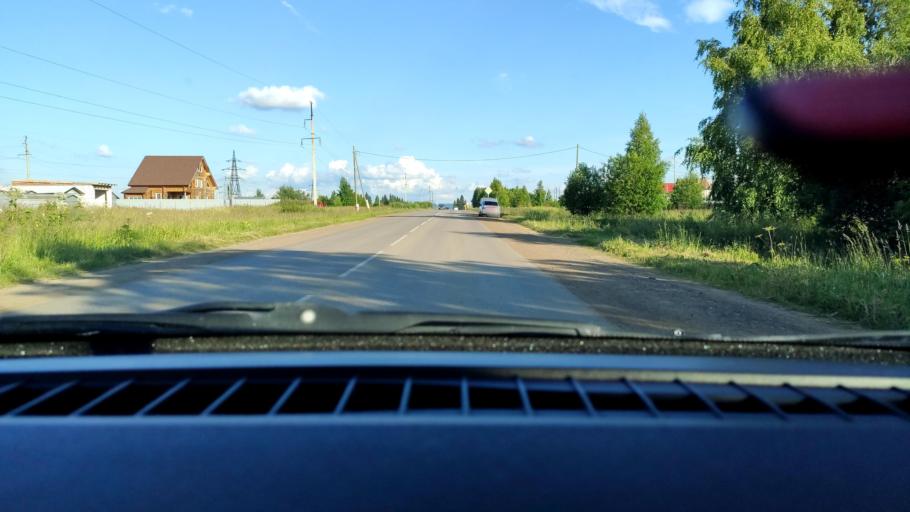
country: RU
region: Perm
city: Kultayevo
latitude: 57.8921
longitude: 55.9180
